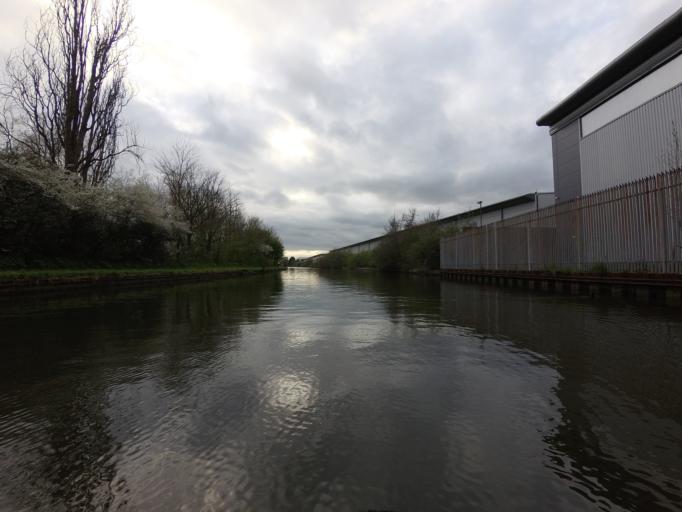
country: GB
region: England
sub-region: Greater London
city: Acton
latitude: 51.5359
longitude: -0.2678
